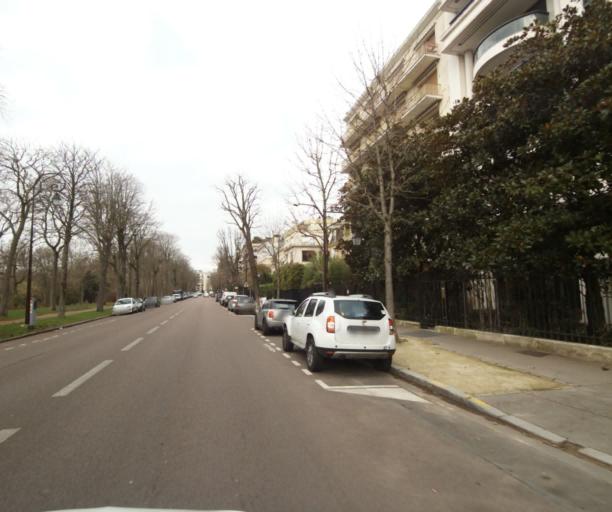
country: FR
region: Ile-de-France
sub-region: Departement des Hauts-de-Seine
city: Neuilly-sur-Seine
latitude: 48.8798
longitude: 2.2635
